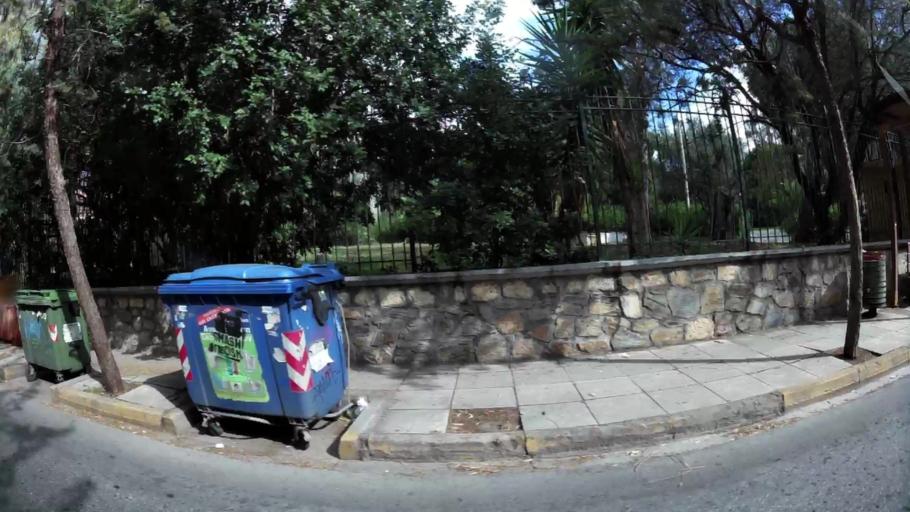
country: GR
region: Attica
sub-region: Nomarchia Athinas
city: Melissia
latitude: 38.0549
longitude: 23.8413
